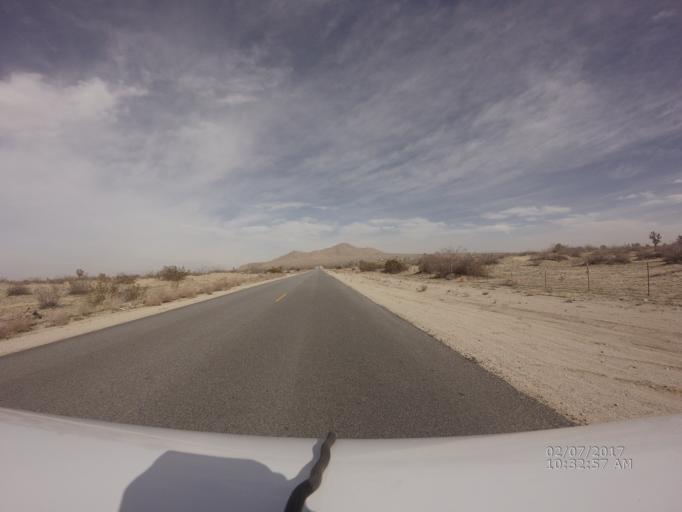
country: US
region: California
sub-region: Los Angeles County
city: Lake Los Angeles
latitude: 34.6806
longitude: -117.8273
